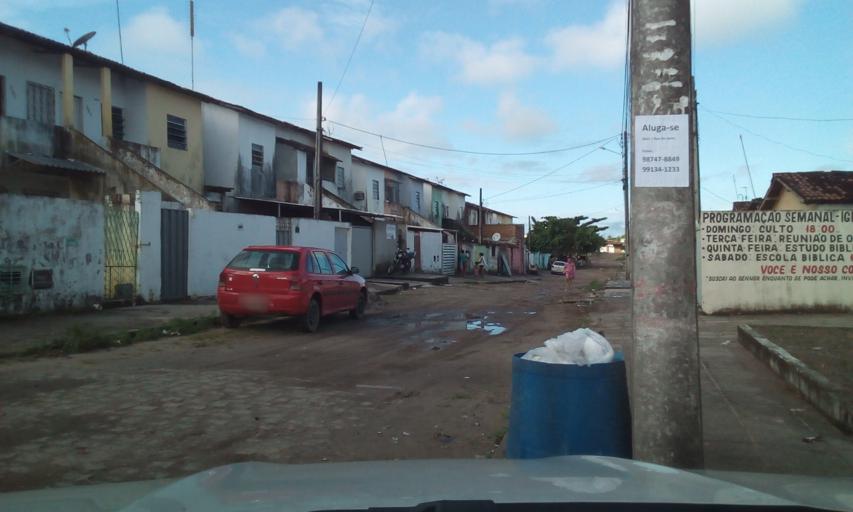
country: BR
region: Paraiba
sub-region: Conde
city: Conde
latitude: -7.2155
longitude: -34.8462
